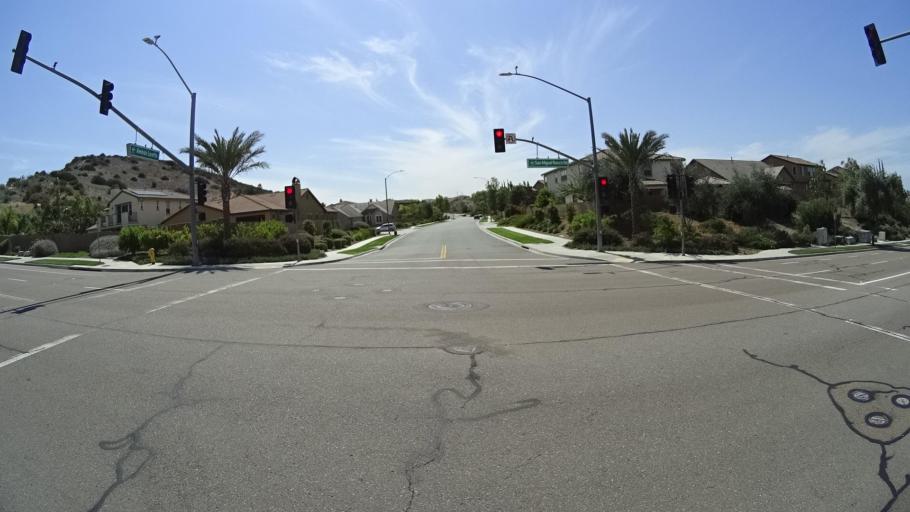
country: US
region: California
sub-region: San Diego County
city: La Presa
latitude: 32.6732
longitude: -116.9909
